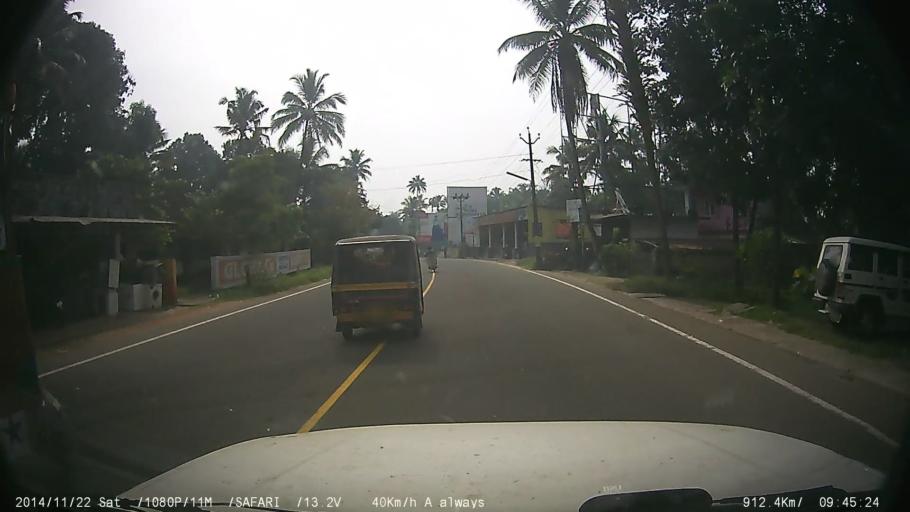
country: IN
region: Kerala
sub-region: Ernakulam
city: Perumpavur
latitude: 10.1391
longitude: 76.4640
